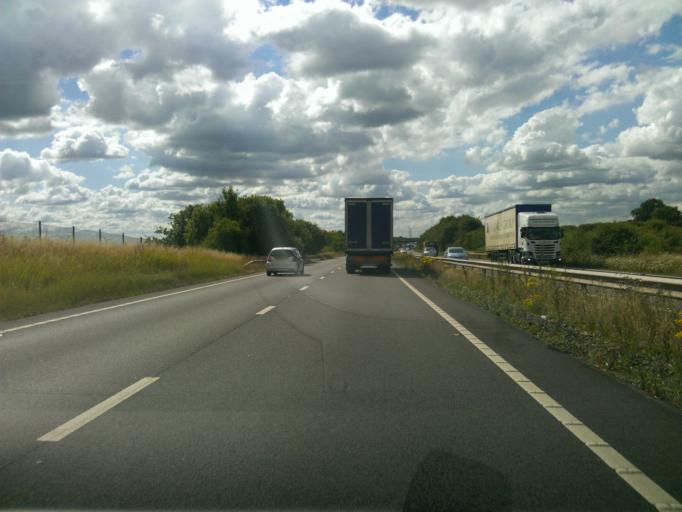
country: GB
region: England
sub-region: Northamptonshire
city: Long Buckby
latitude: 52.3923
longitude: -1.0968
